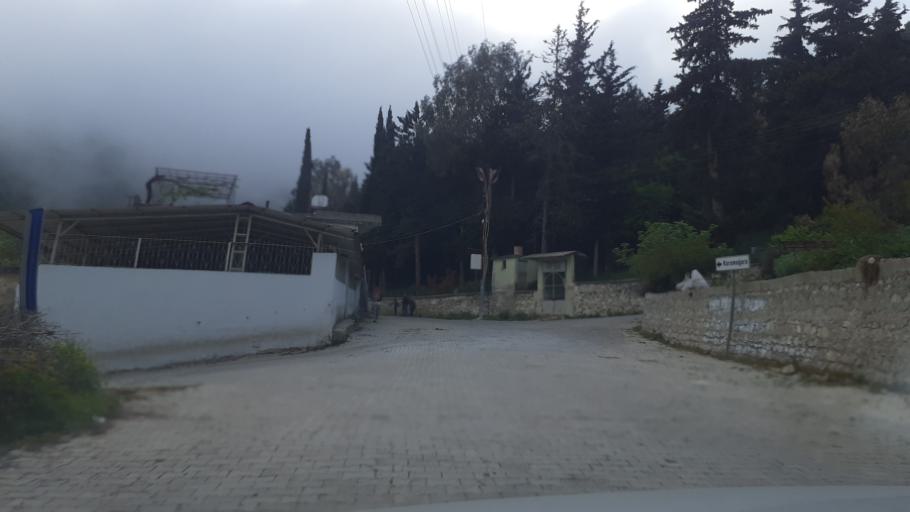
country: TR
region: Hatay
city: Yeditepe
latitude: 35.9680
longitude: 36.0131
